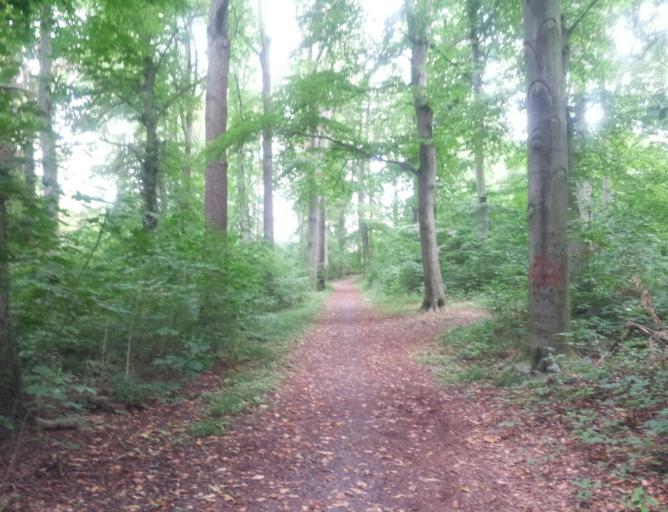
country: DE
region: Lower Saxony
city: Goslar
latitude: 51.9120
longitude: 10.4337
